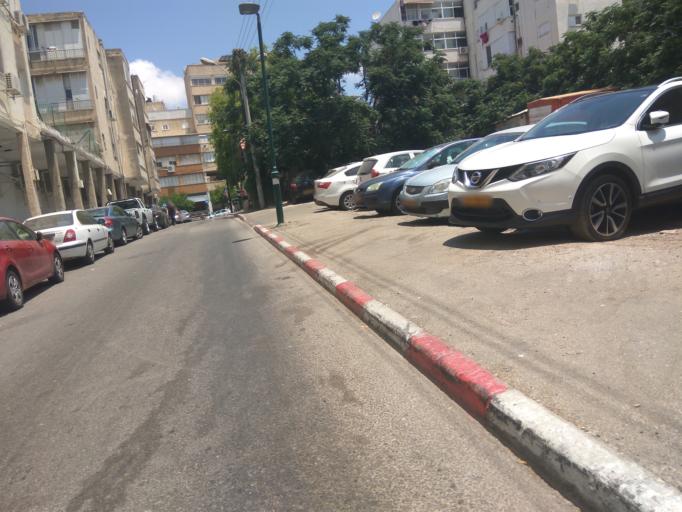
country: IL
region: Central District
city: Rishon LeZiyyon
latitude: 31.9635
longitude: 34.8061
